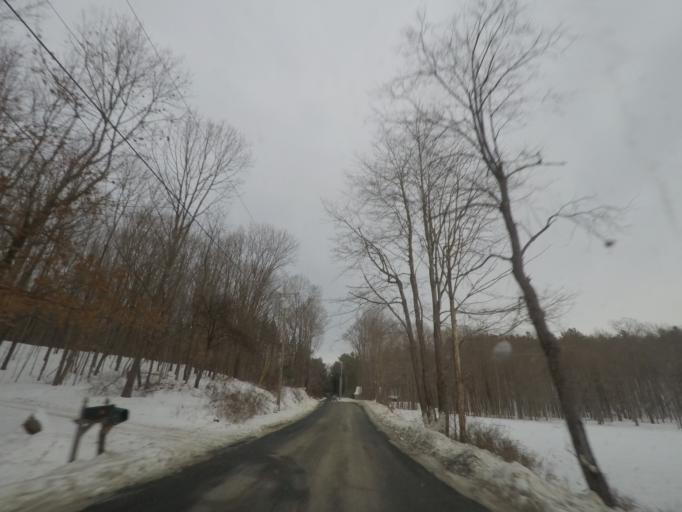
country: US
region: New York
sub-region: Rensselaer County
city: Nassau
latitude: 42.5758
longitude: -73.5847
